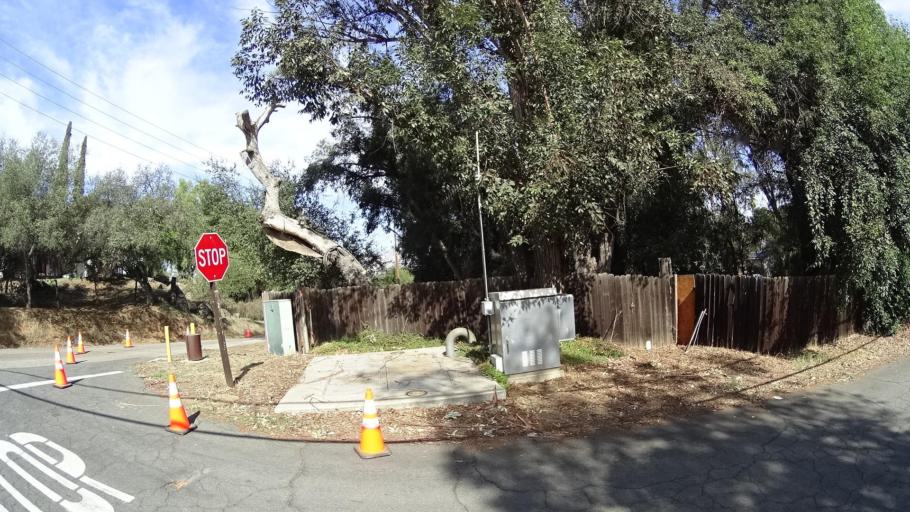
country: US
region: California
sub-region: San Diego County
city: Alpine
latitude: 32.8281
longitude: -116.7887
